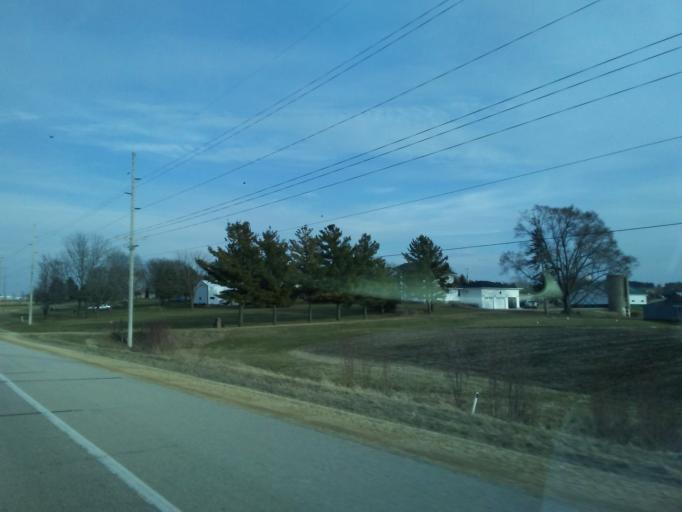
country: US
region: Wisconsin
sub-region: Iowa County
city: Dodgeville
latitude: 42.9747
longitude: -90.1521
